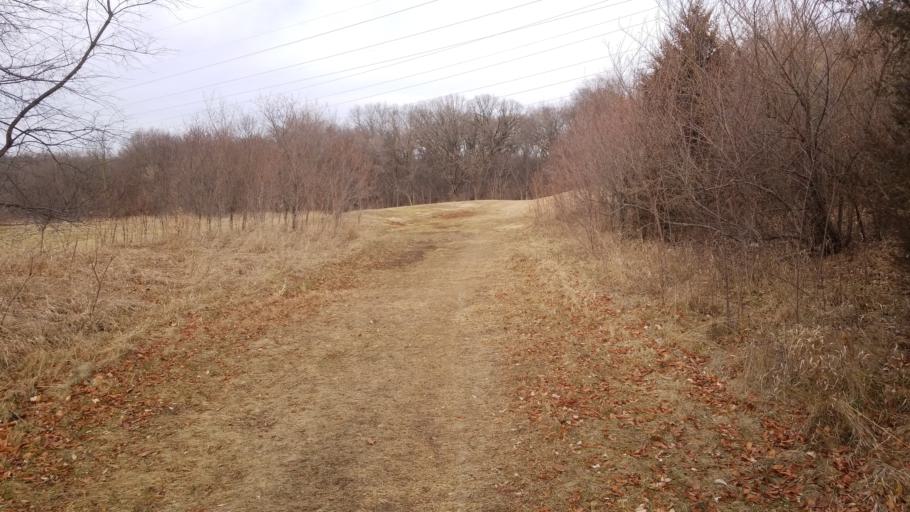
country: US
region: Nebraska
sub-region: Sarpy County
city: Offutt Air Force Base
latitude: 41.1635
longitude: -95.9602
